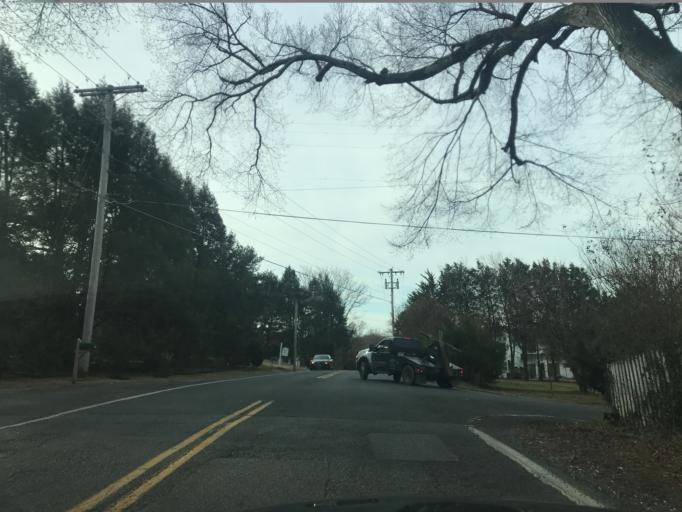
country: US
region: Maryland
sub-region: Charles County
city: Hughesville
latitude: 38.5549
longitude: -76.8423
